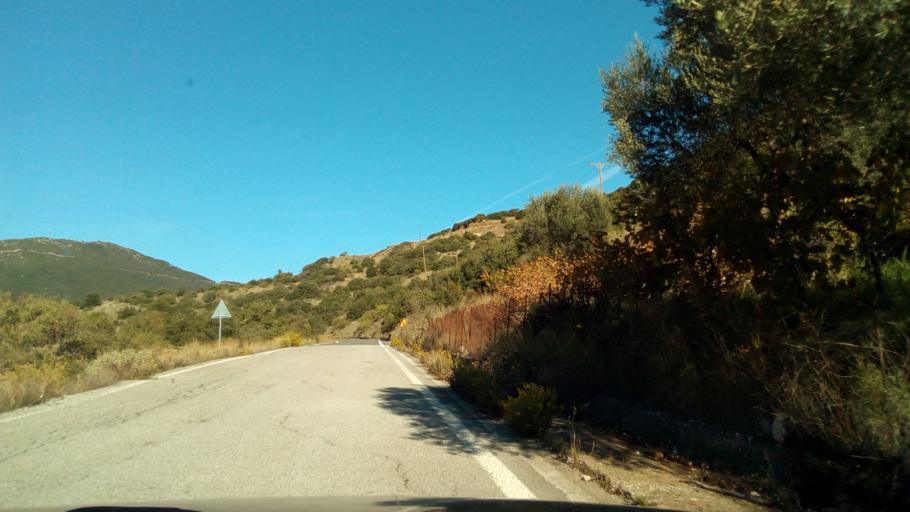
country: GR
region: West Greece
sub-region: Nomos Aitolias kai Akarnanias
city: Nafpaktos
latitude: 38.4829
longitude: 21.8568
